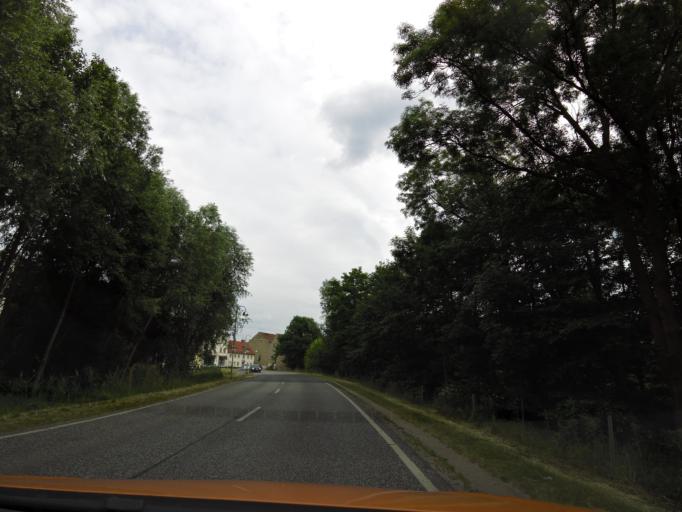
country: DE
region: Brandenburg
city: Zossen
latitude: 52.2141
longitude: 13.4515
